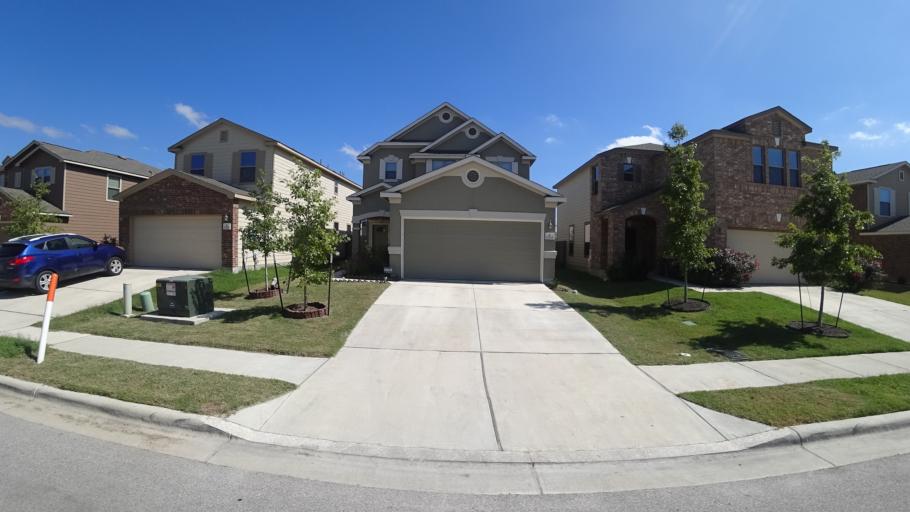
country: US
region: Texas
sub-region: Travis County
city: Manor
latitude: 30.3481
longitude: -97.6201
